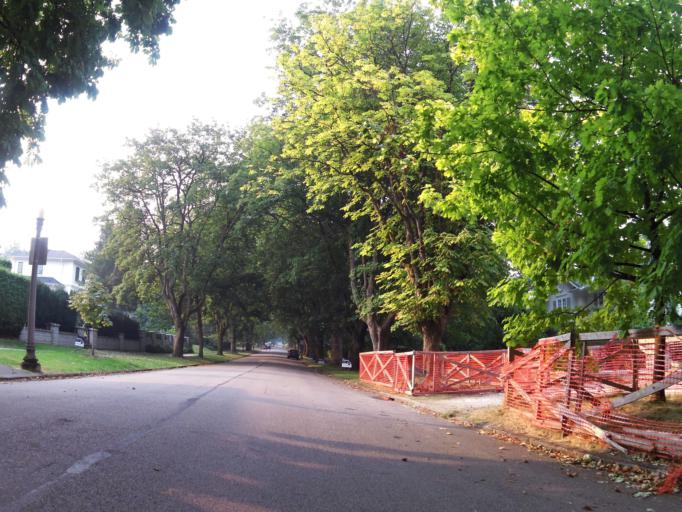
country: CA
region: British Columbia
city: Vancouver
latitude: 49.2450
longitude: -123.1455
